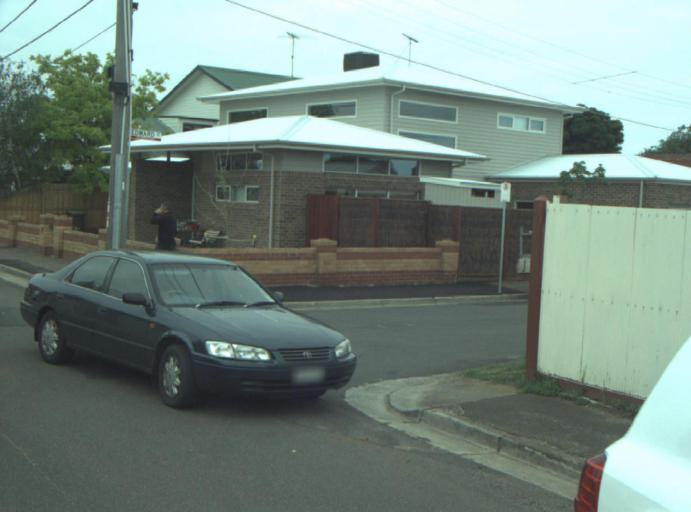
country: AU
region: Victoria
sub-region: Greater Geelong
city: Geelong West
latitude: -38.1240
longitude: 144.3570
